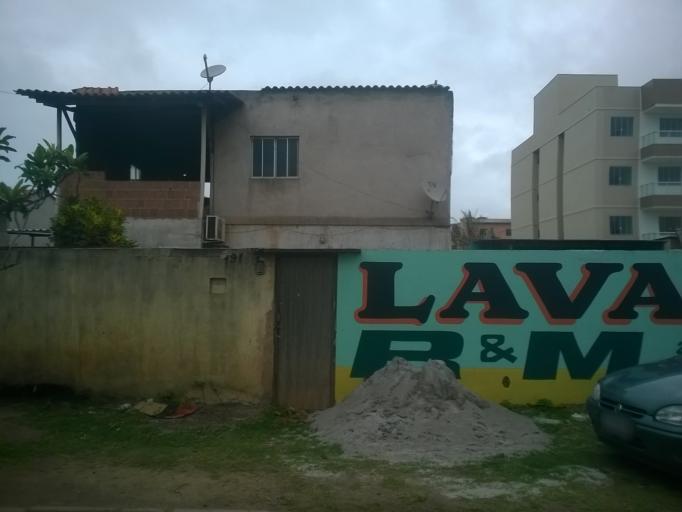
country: BR
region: Espirito Santo
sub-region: Vila Velha
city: Vila Velha
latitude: -20.4283
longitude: -40.3374
